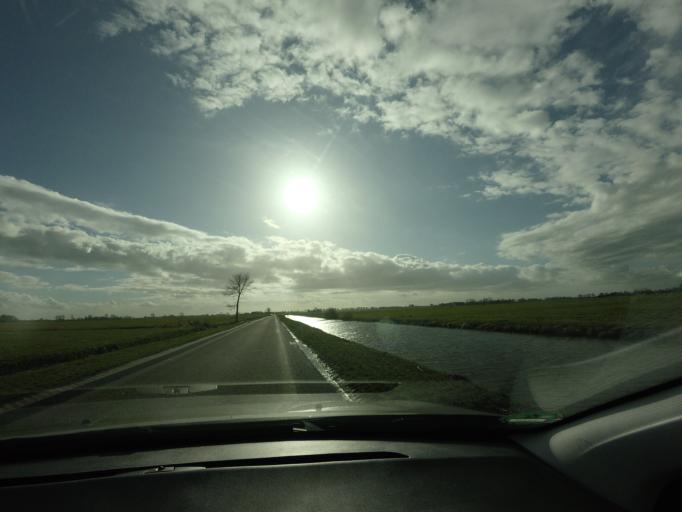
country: NL
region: Friesland
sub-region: Sudwest Fryslan
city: Oppenhuizen
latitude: 53.0482
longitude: 5.7229
